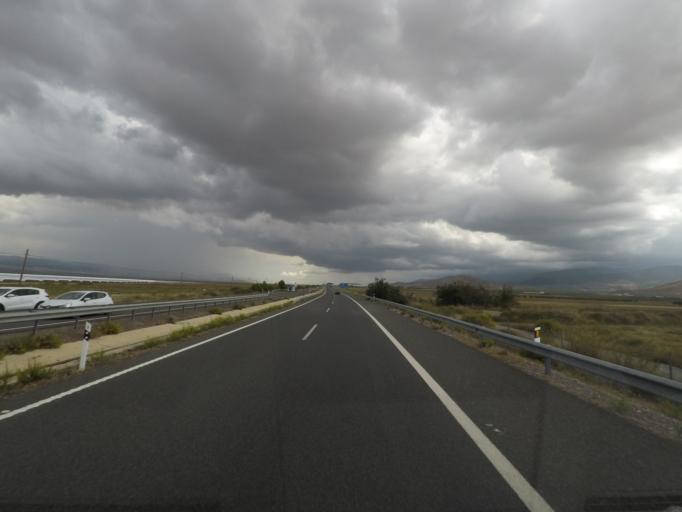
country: ES
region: Andalusia
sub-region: Provincia de Granada
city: Ferreira
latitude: 37.2104
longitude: -3.0649
